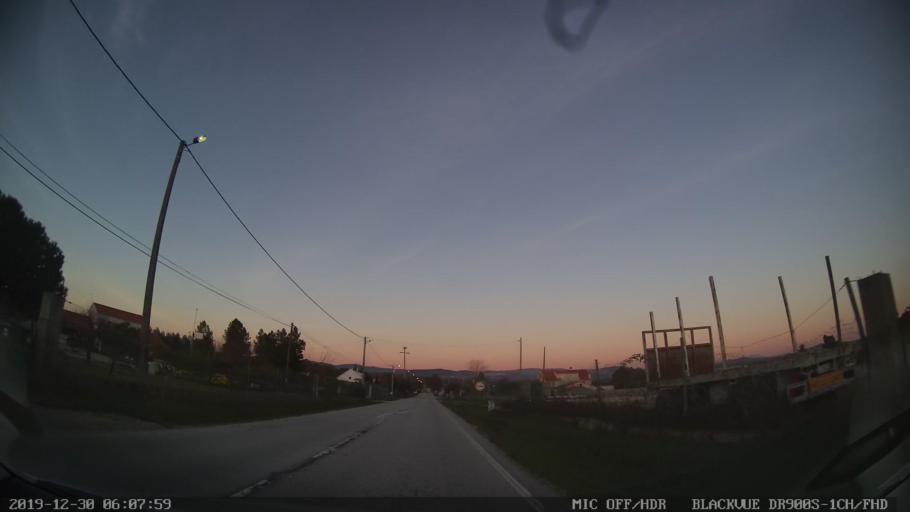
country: PT
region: Castelo Branco
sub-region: Penamacor
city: Penamacor
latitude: 40.1119
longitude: -7.2216
